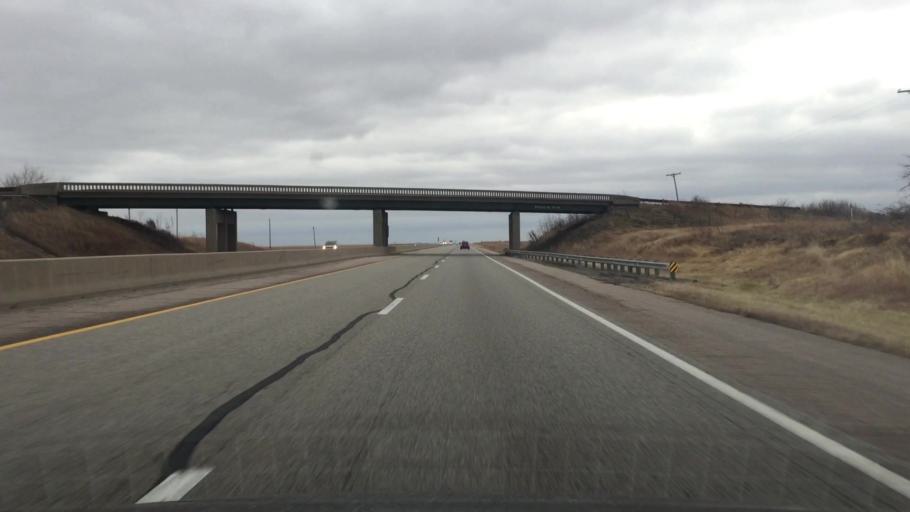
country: US
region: Kansas
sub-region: Butler County
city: El Dorado
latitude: 37.9128
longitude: -96.8065
